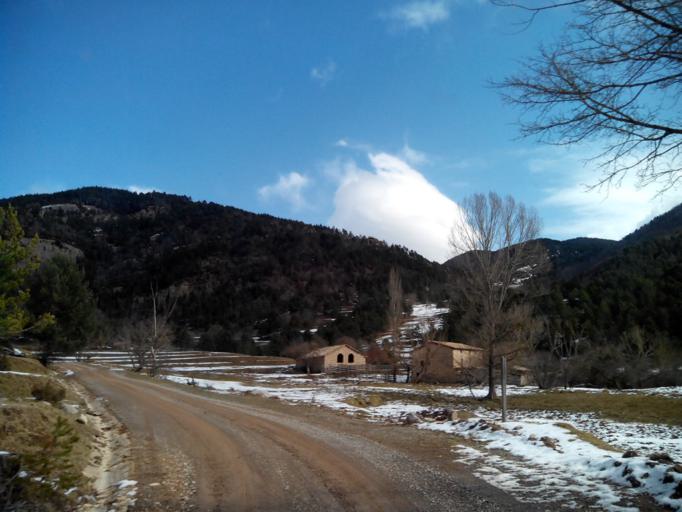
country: ES
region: Catalonia
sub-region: Provincia de Barcelona
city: Vilada
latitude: 42.1795
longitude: 1.9262
